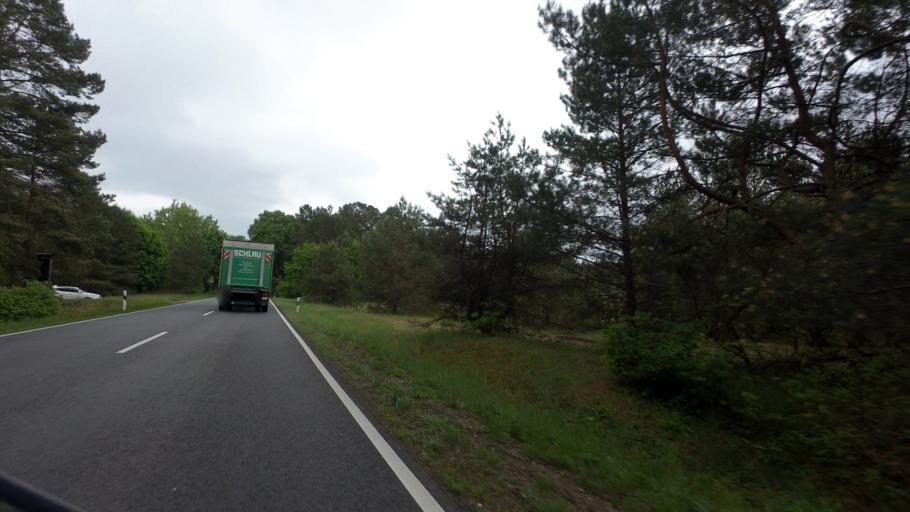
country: DE
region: Brandenburg
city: Furstenberg
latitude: 53.1986
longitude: 13.1369
